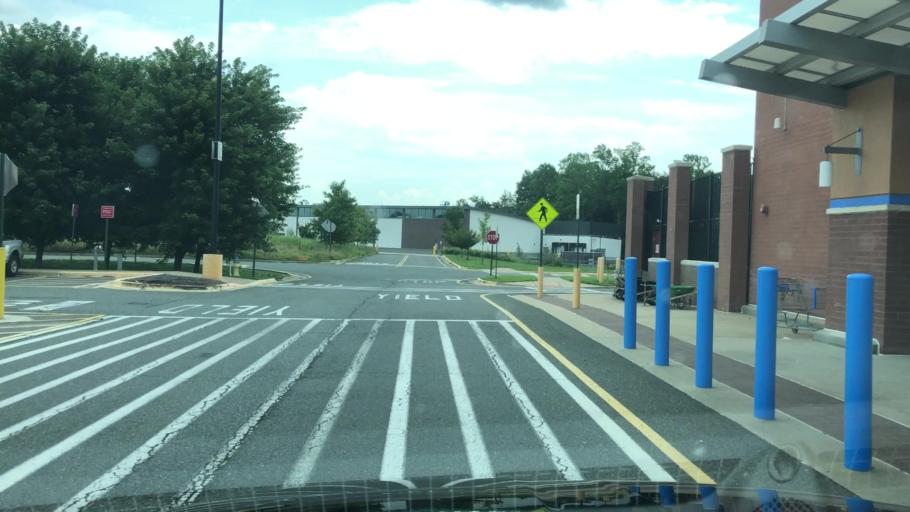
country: US
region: Virginia
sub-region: Stafford County
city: Falmouth
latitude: 38.3695
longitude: -77.5282
